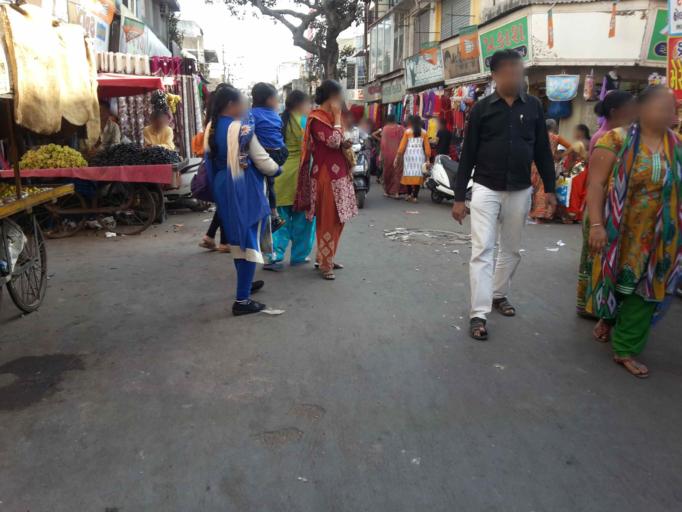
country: IN
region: Gujarat
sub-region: Rajkot
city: Rajkot
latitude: 22.2879
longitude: 70.8081
